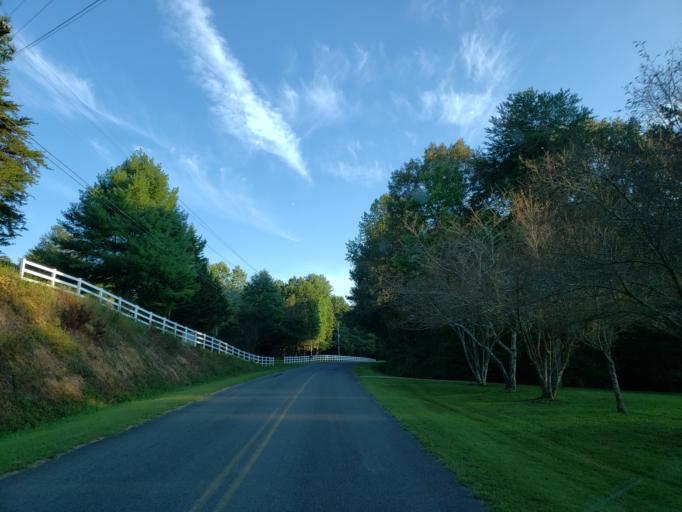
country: US
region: Georgia
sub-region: Gilmer County
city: Ellijay
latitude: 34.6605
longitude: -84.3367
